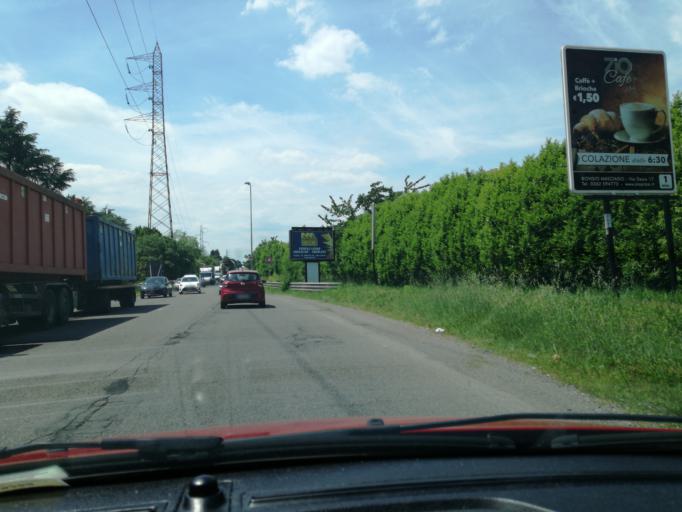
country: IT
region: Lombardy
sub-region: Provincia di Monza e Brianza
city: Bovisio-Masciago
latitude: 45.6168
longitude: 9.1464
